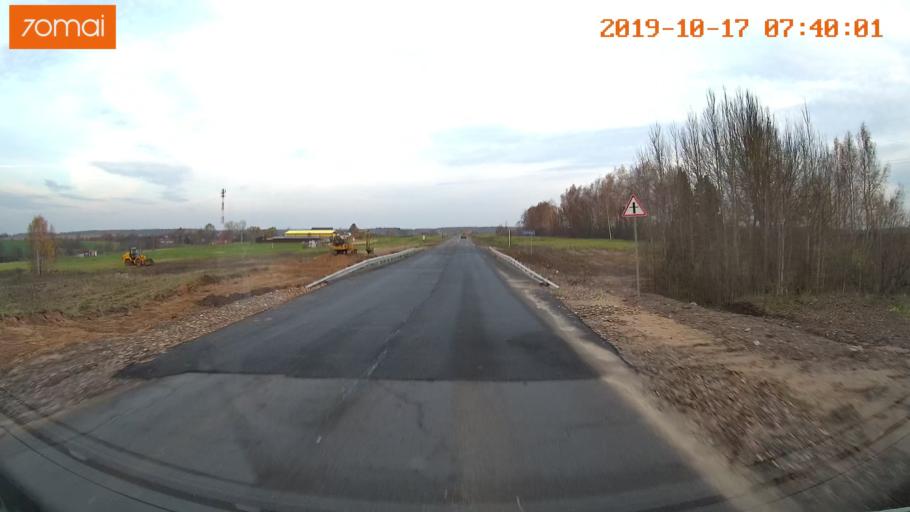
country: RU
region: Vladimir
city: Yur'yev-Pol'skiy
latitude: 56.4683
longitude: 39.8375
